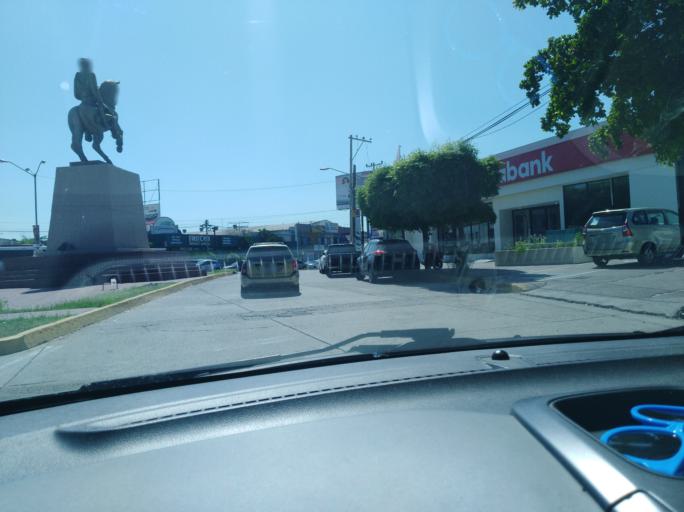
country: MX
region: Sinaloa
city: Culiacan
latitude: 24.7935
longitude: -107.4130
